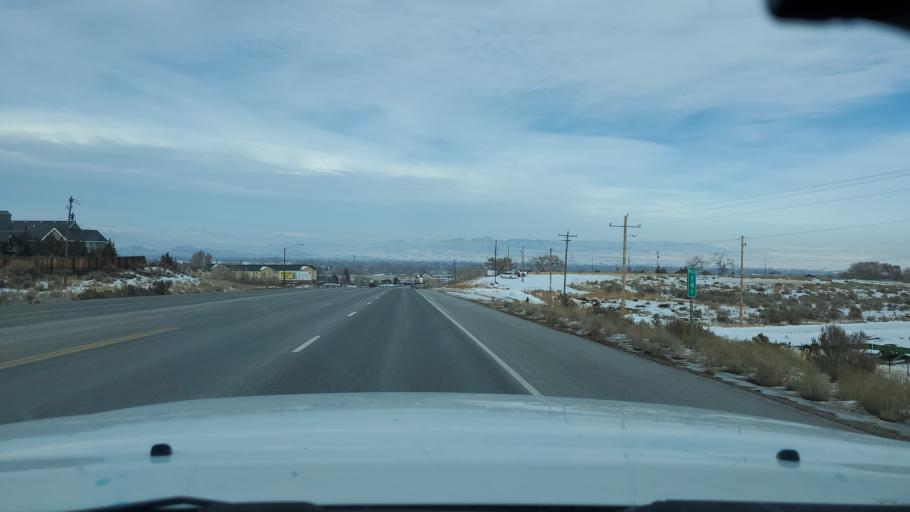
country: US
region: Utah
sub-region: Uintah County
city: Maeser
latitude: 40.4289
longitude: -109.5769
